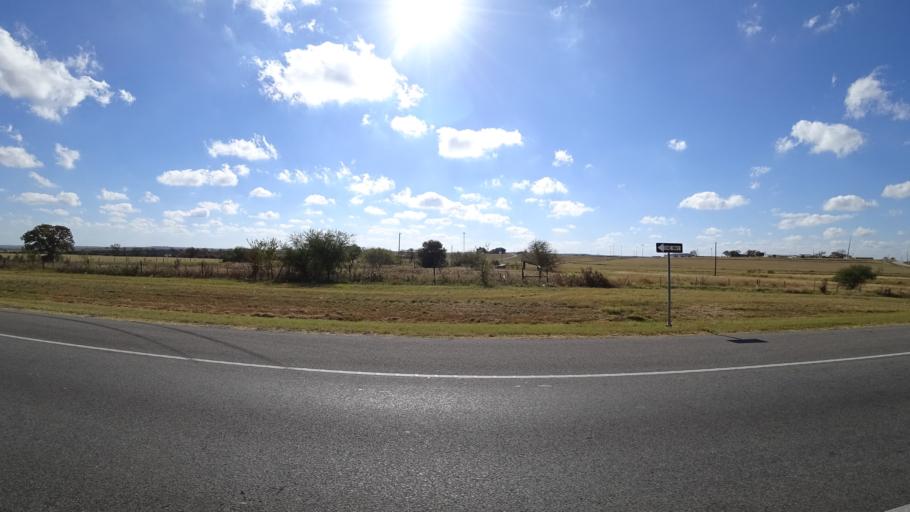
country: US
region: Texas
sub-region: Travis County
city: Garfield
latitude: 30.1865
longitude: -97.6061
